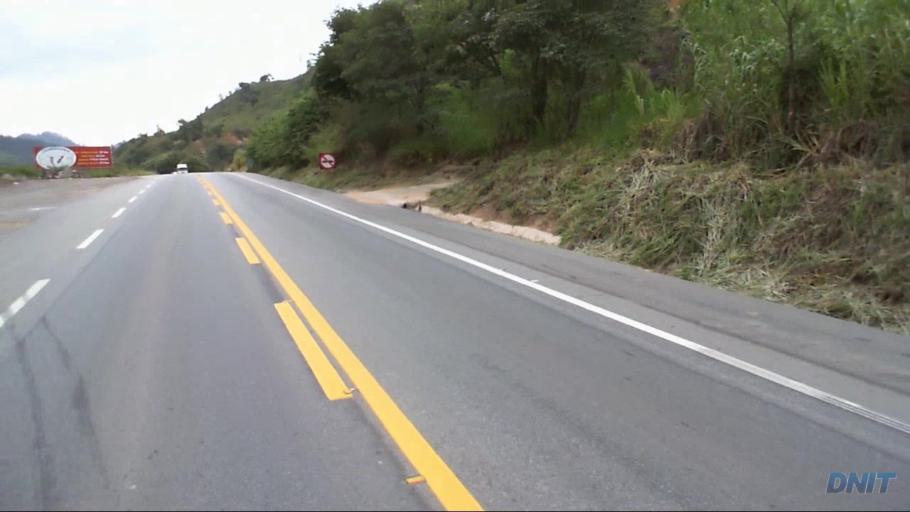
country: BR
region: Minas Gerais
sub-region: Timoteo
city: Timoteo
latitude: -19.6139
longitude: -42.7705
